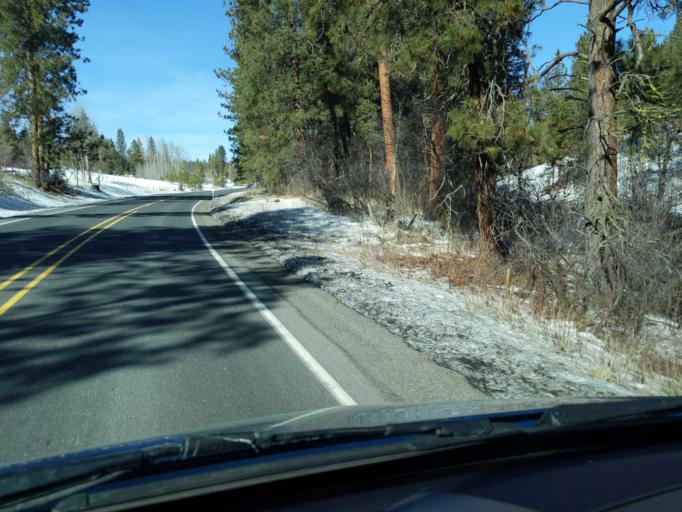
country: US
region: Oregon
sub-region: Grant County
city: John Day
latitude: 44.8952
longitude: -119.0146
